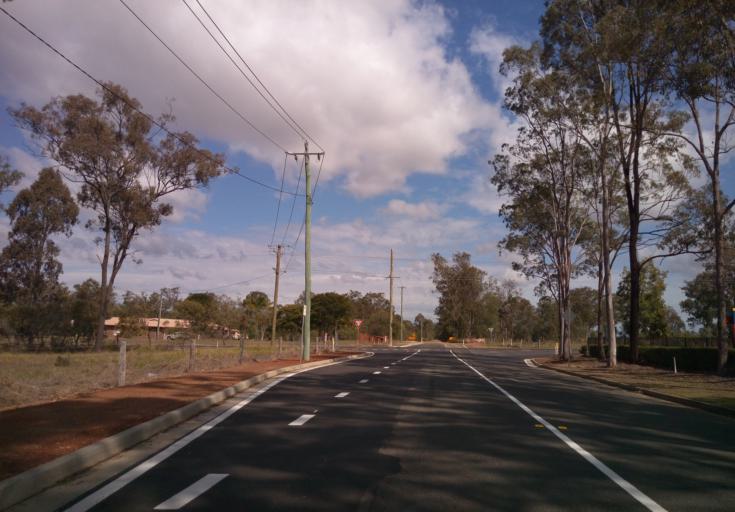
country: AU
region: Queensland
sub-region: Ipswich
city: Brassall
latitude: -27.5905
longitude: 152.7043
